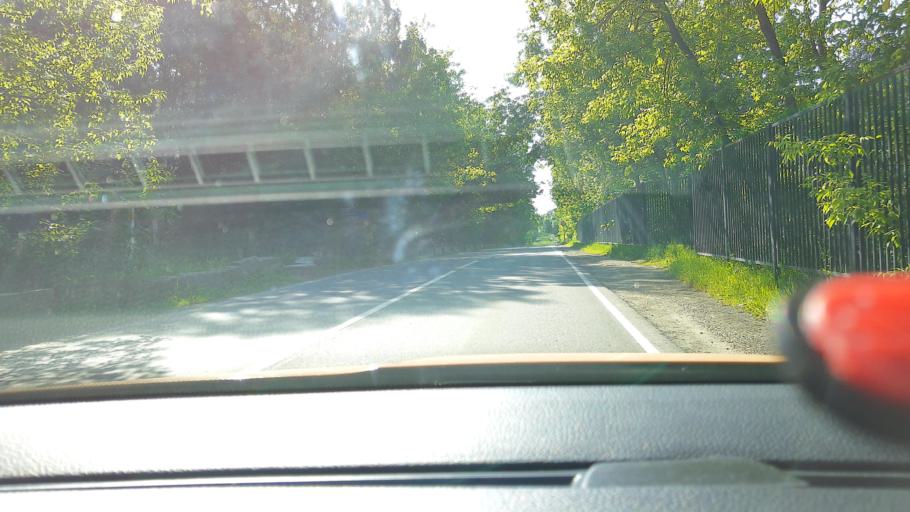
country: RU
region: Moskovskaya
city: Zarech'ye
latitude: 55.6609
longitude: 37.3935
